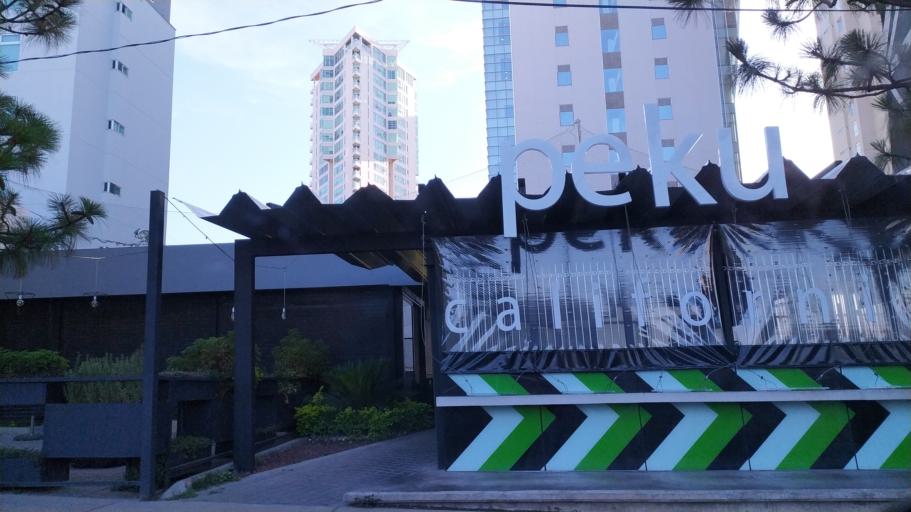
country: MX
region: Jalisco
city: Zapopan2
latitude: 20.7074
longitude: -103.4159
